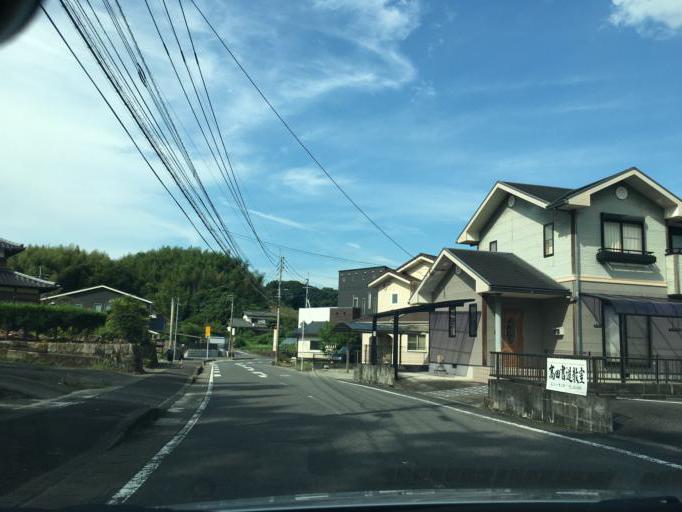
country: JP
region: Saga Prefecture
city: Takeocho-takeo
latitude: 33.1885
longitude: 130.0326
